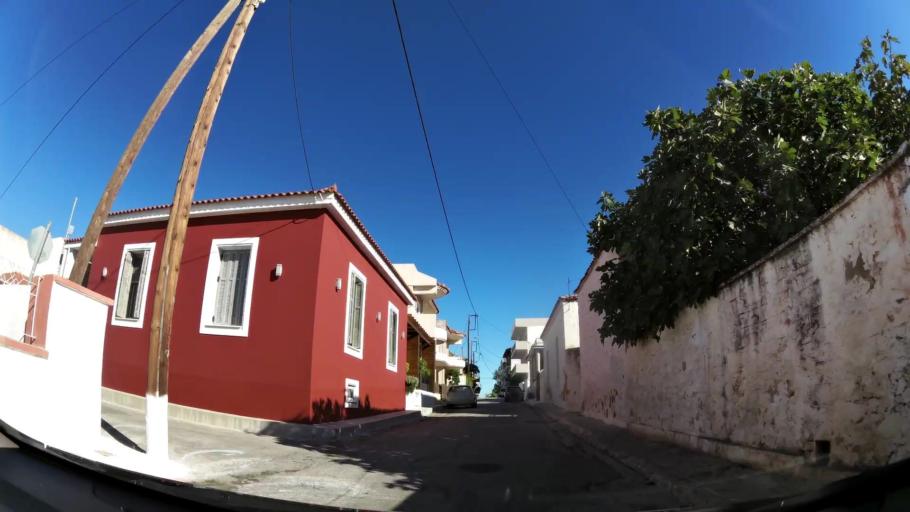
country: GR
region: Attica
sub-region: Nomarchia Anatolikis Attikis
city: Koropi
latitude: 37.9008
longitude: 23.8694
